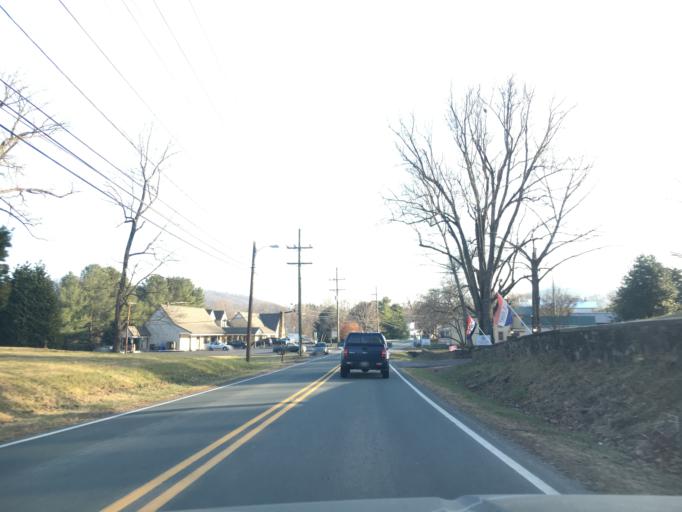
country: US
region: Virginia
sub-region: Rappahannock County
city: Washington
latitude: 38.7675
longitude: -78.1013
